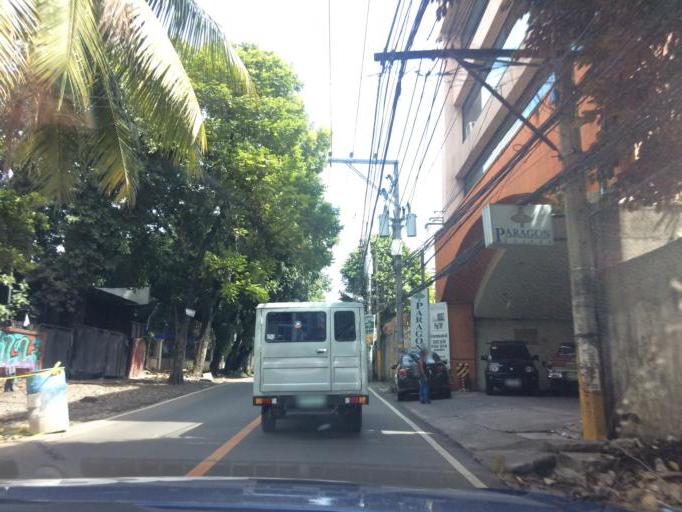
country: PH
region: Central Visayas
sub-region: Province of Cebu
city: Cebu City
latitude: 10.3147
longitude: 123.8941
